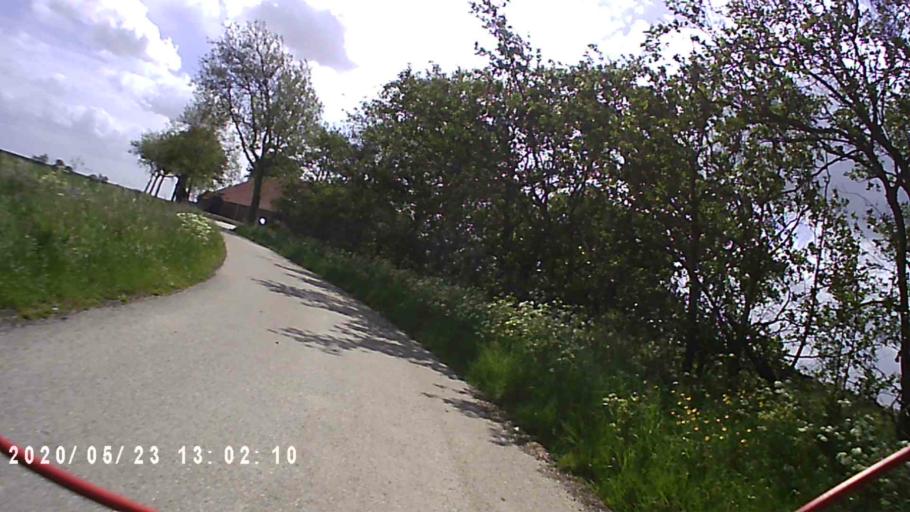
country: NL
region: Groningen
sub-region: Gemeente  Oldambt
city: Winschoten
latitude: 53.2912
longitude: 7.0674
